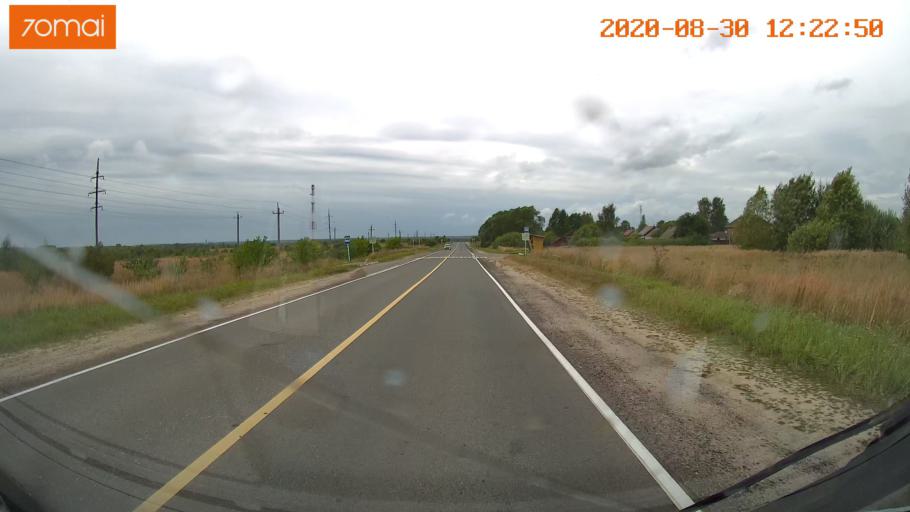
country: RU
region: Ivanovo
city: Yur'yevets
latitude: 57.3312
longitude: 42.8405
